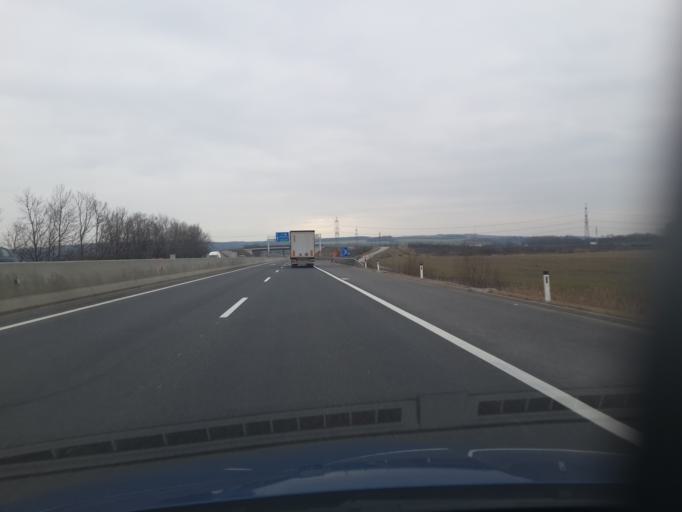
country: AT
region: Burgenland
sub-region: Politischer Bezirk Neusiedl am See
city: Parndorf
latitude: 48.0240
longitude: 16.8457
